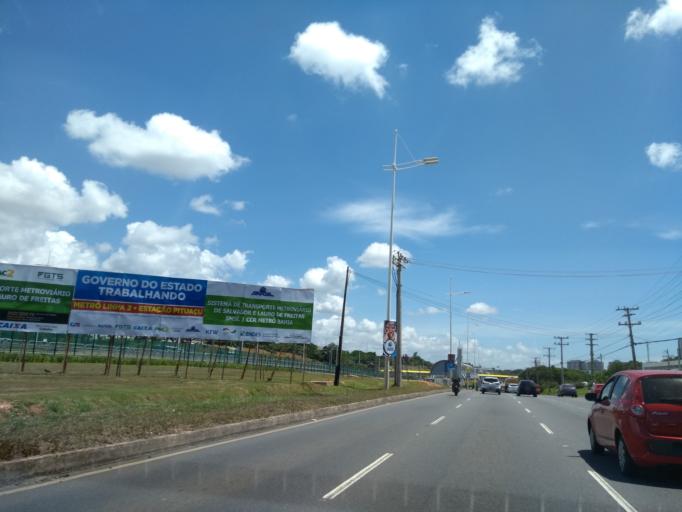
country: BR
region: Bahia
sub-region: Salvador
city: Salvador
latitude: -12.9490
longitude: -38.4236
